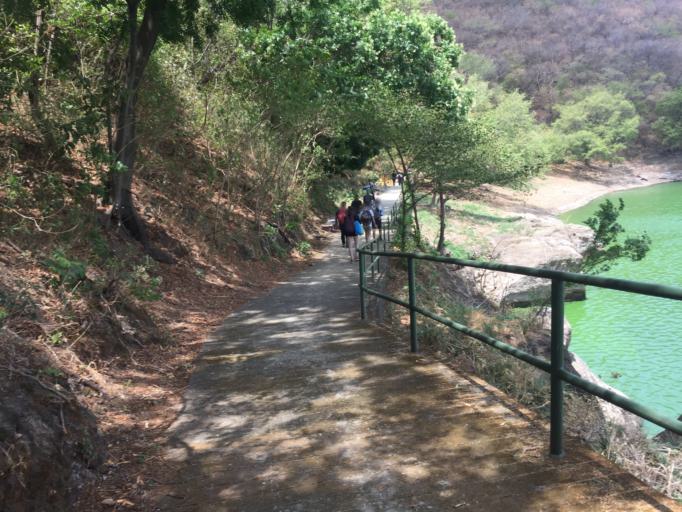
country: NI
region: Managua
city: Managua
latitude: 12.1376
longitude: -86.2712
